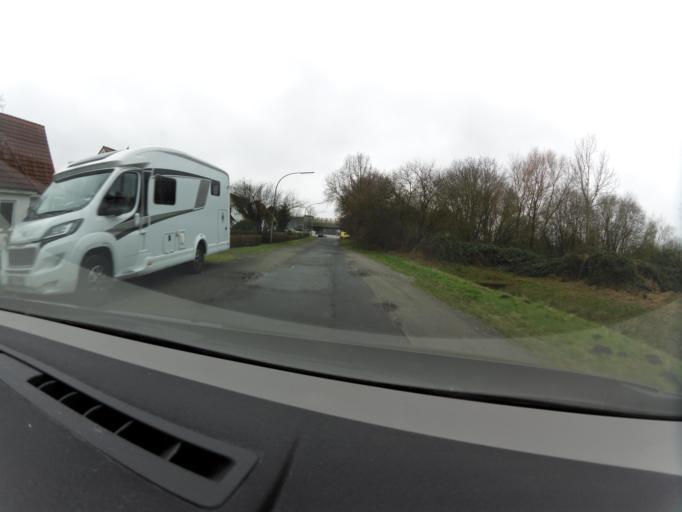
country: DE
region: Bremen
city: Bremerhaven
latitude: 53.5482
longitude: 8.5992
